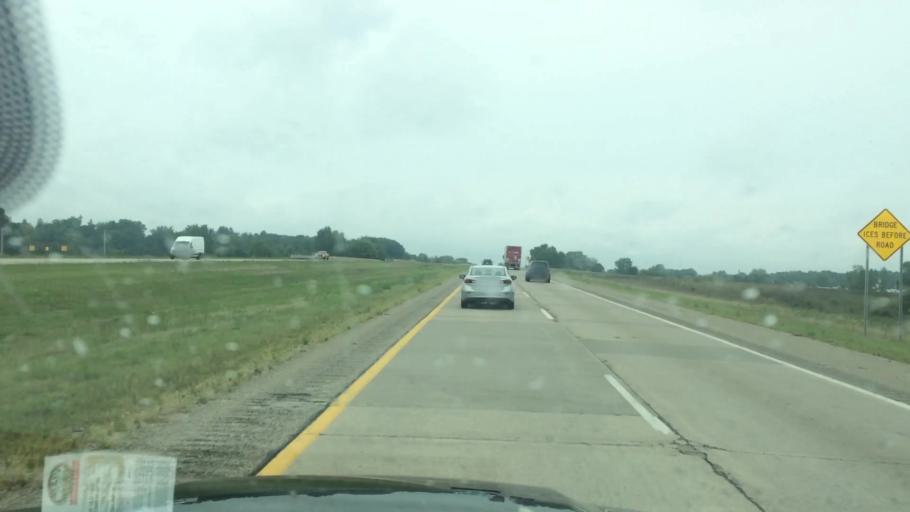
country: US
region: Michigan
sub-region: Eaton County
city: Charlotte
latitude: 42.5727
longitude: -84.8201
